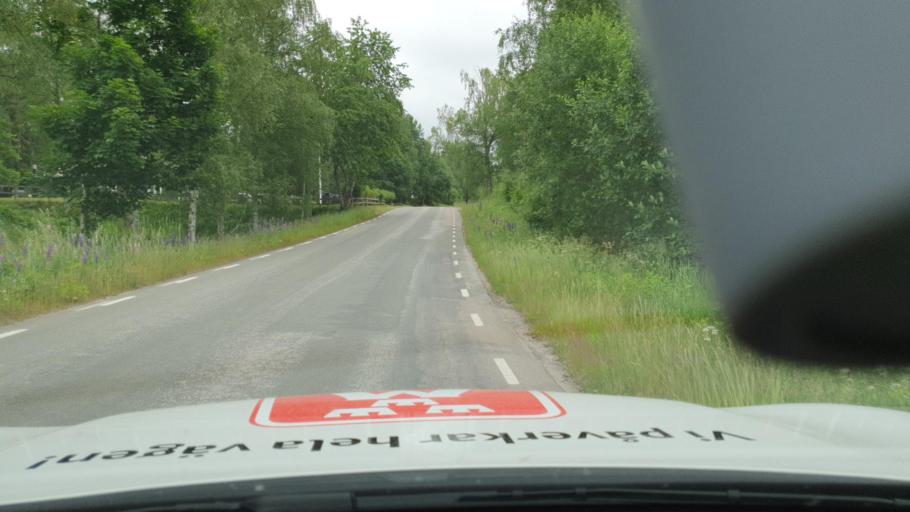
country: SE
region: Vaestra Goetaland
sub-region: Tibro Kommun
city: Tibro
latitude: 58.4145
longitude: 14.2349
